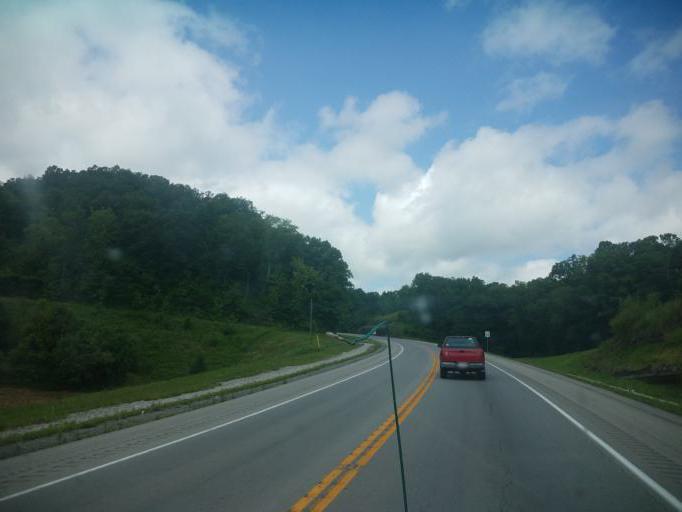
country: US
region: Kentucky
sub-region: Cumberland County
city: Burkesville
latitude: 36.8001
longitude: -85.3775
